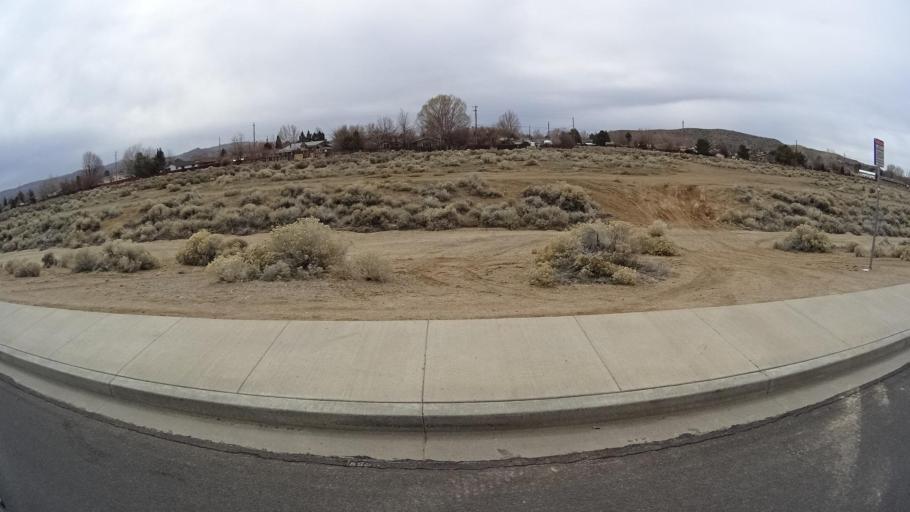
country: US
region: Nevada
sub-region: Washoe County
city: Spanish Springs
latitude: 39.6365
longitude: -119.7226
